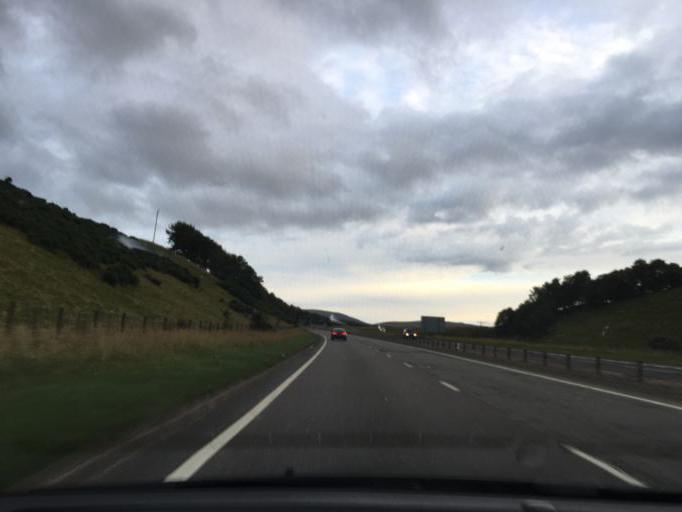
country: GB
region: Scotland
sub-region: Highland
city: Inverness
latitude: 57.4118
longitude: -4.1357
